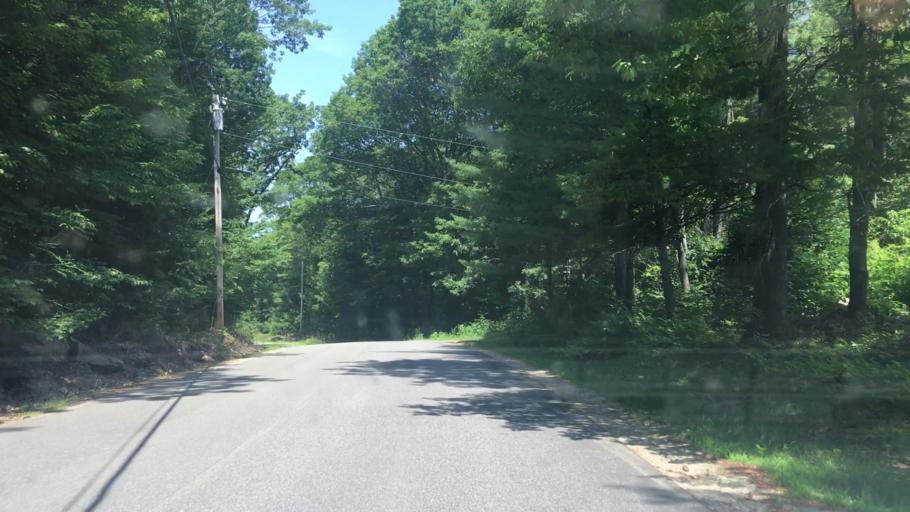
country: US
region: Maine
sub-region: Kennebec County
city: Monmouth
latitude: 44.2790
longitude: -70.0518
